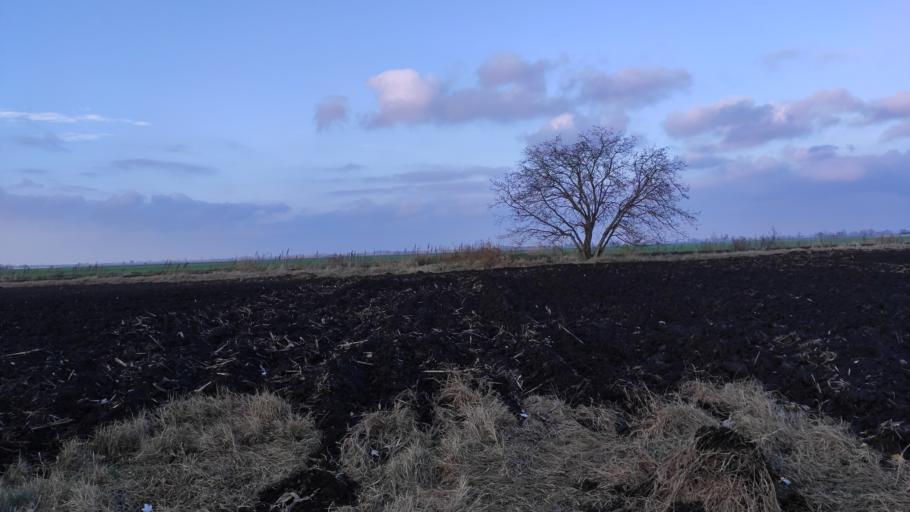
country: HU
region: Bekes
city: Mezobereny
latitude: 46.7649
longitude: 21.0517
